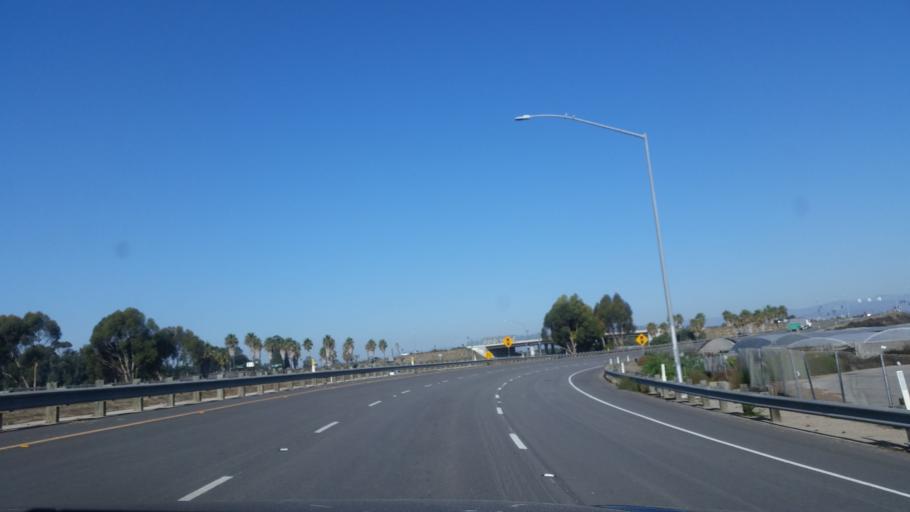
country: US
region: California
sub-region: Ventura County
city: Oxnard
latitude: 34.1634
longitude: -119.1401
